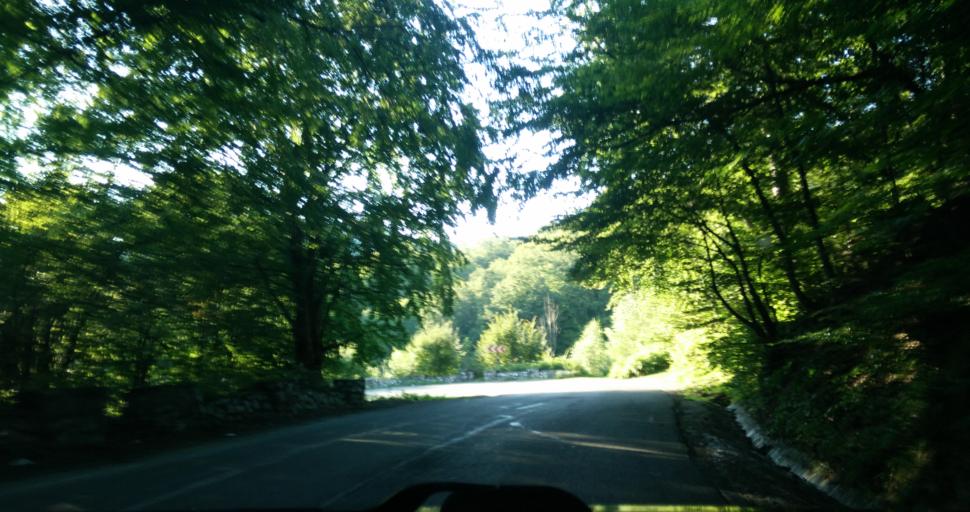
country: RO
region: Bihor
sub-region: Oras Nucet
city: Nucet
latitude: 46.4877
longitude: 22.6052
